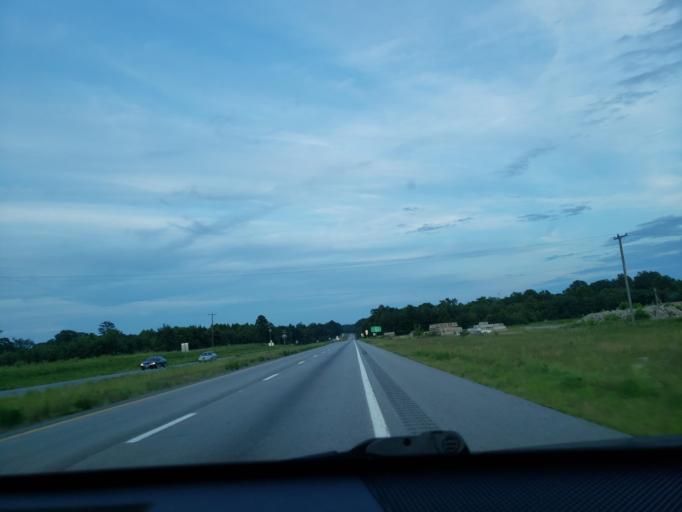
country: US
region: Virginia
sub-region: Southampton County
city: Courtland
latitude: 36.7027
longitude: -77.2599
